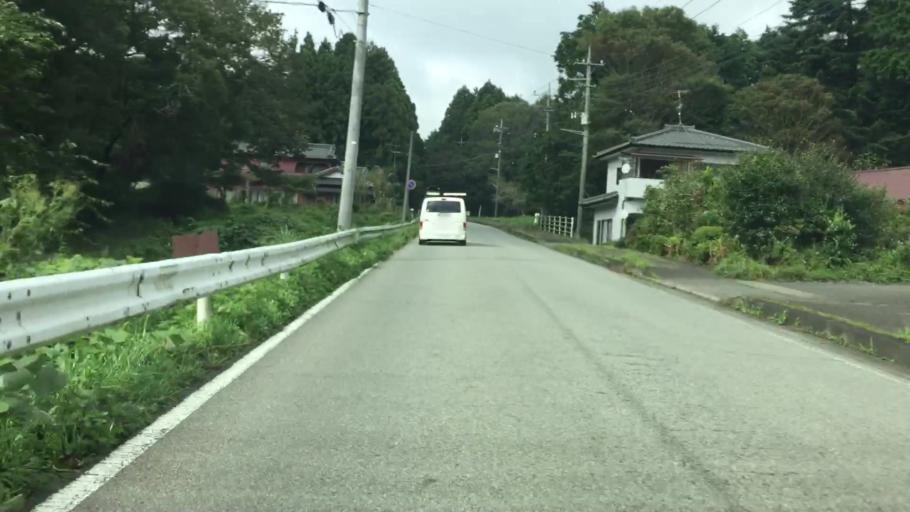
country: JP
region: Shizuoka
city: Fujinomiya
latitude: 35.3474
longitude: 138.5957
